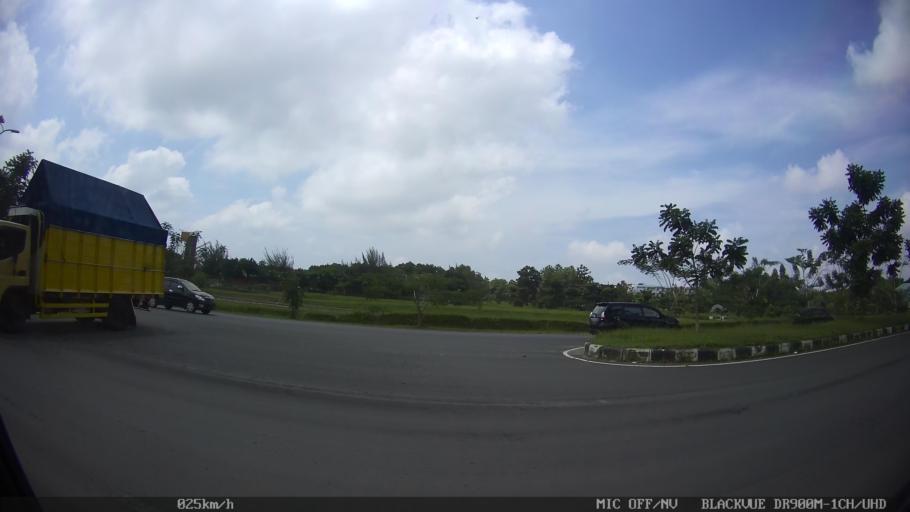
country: ID
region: Lampung
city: Kedaton
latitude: -5.3576
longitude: 105.3110
